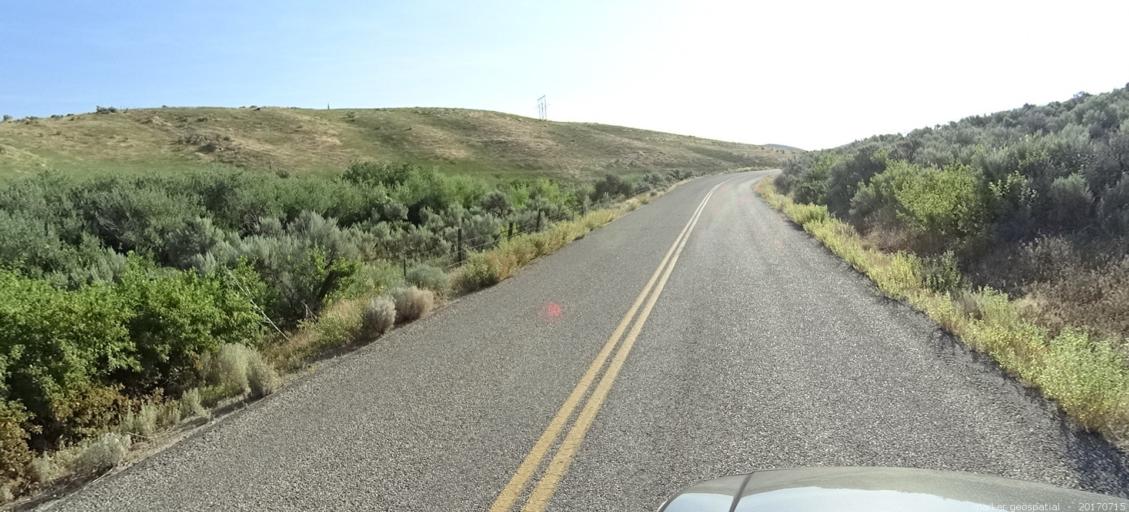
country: US
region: Idaho
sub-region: Ada County
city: Boise
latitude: 43.4790
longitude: -115.9892
